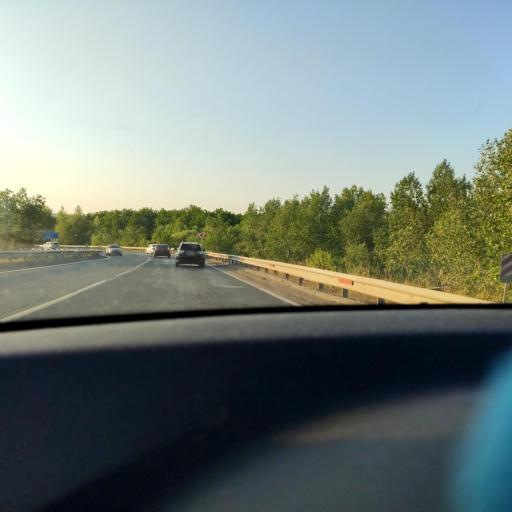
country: RU
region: Samara
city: Kinel'
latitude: 53.2524
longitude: 50.5916
